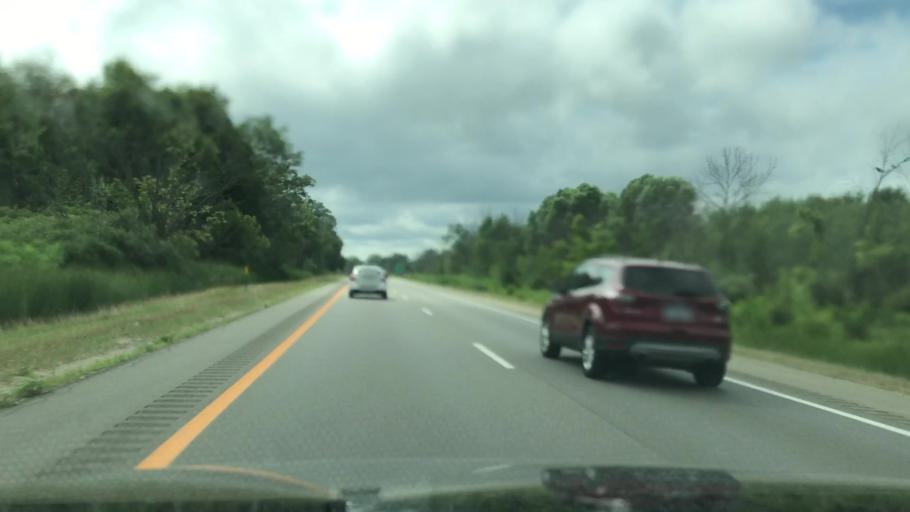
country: US
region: Michigan
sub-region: Ottawa County
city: Coopersville
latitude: 43.0728
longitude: -86.0383
